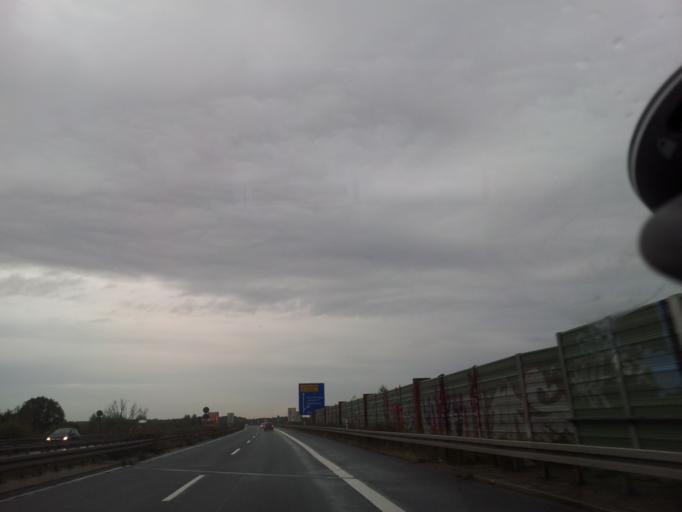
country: DE
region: Lower Saxony
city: Vordorf
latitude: 52.3247
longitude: 10.5249
